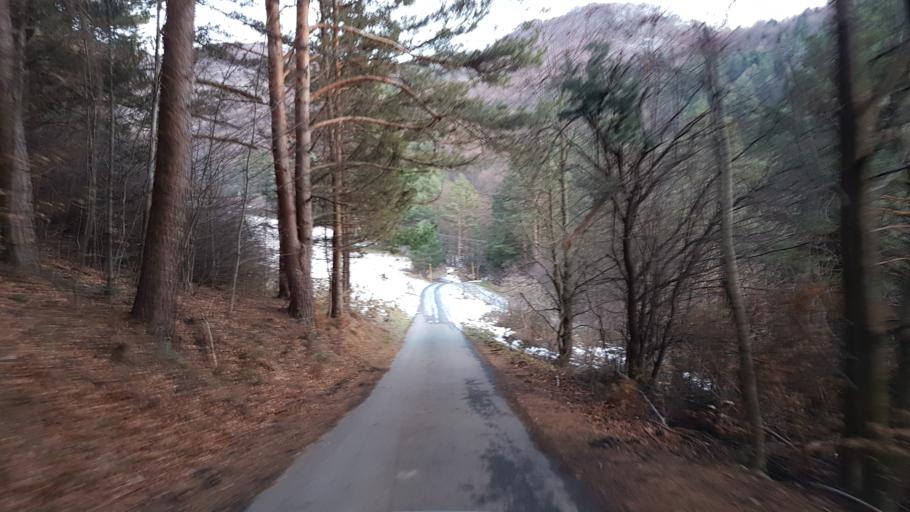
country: PL
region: Lesser Poland Voivodeship
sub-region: Powiat nowosadecki
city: Rytro
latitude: 49.4895
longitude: 20.6893
